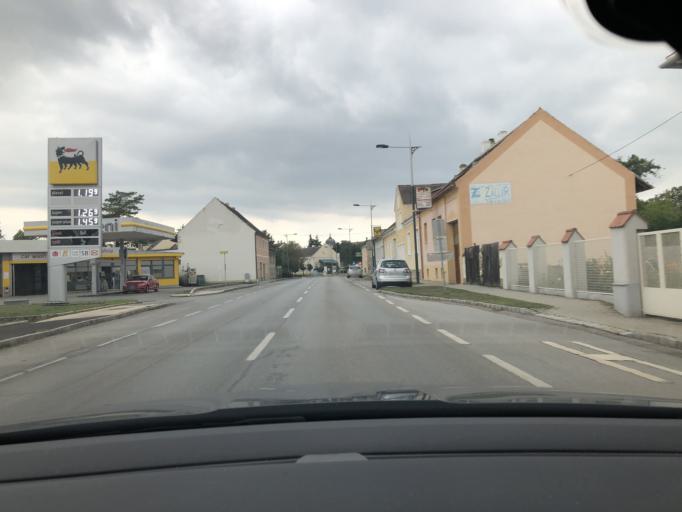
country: AT
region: Lower Austria
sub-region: Politischer Bezirk Mistelbach
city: Laa an der Thaya
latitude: 48.7186
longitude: 16.3958
